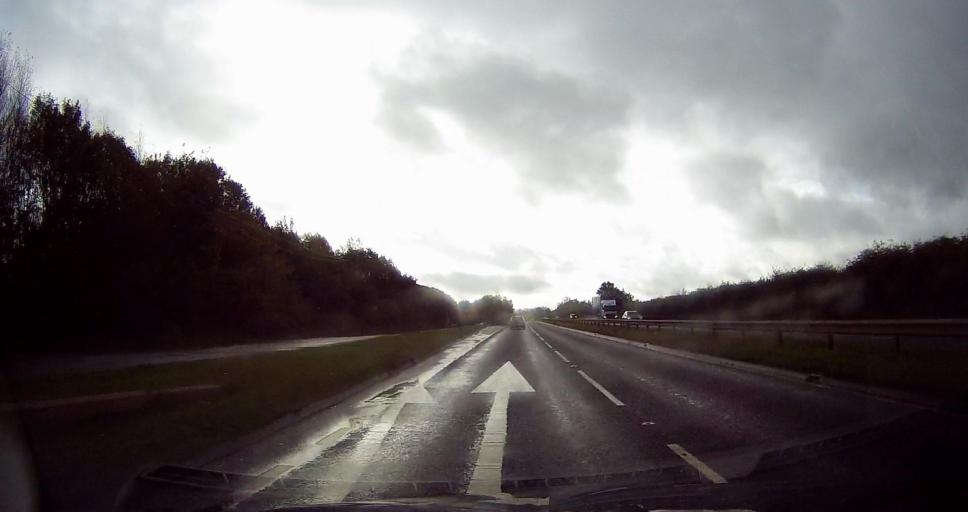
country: GB
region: England
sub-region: City and Borough of Birmingham
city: Sutton Coldfield
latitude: 52.6041
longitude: -1.7953
